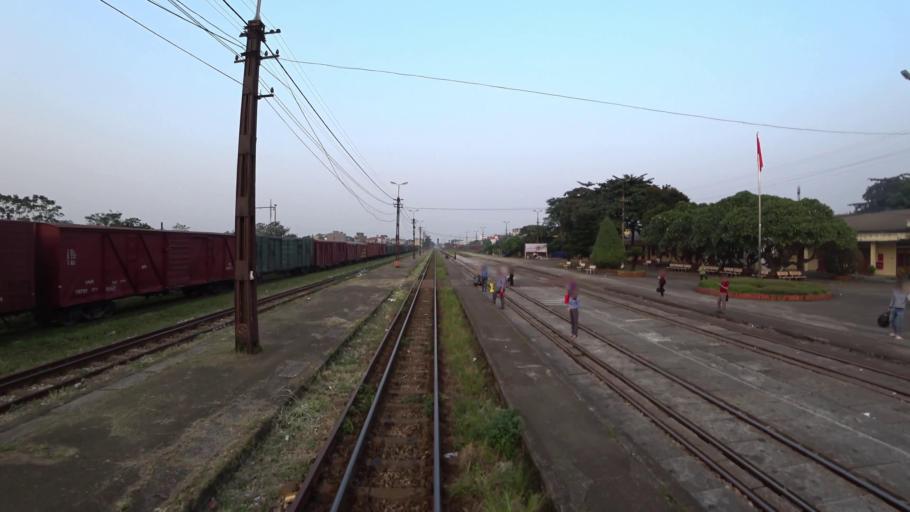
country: VN
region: Ha Noi
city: Dong Anh
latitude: 21.0978
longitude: 105.9091
